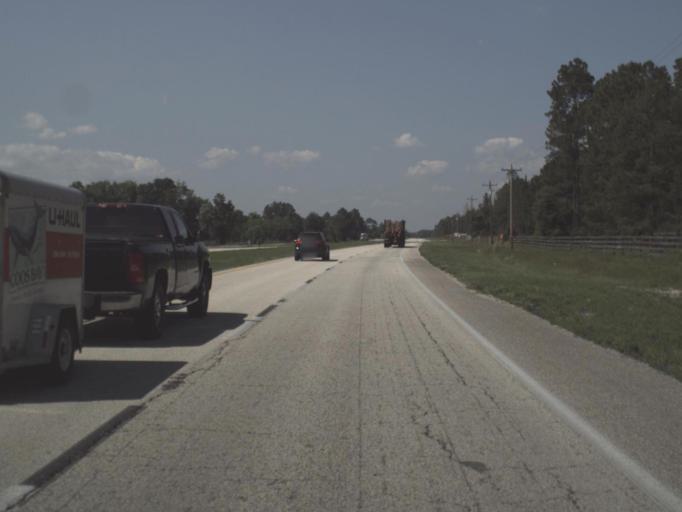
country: US
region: Florida
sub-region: Alachua County
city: Hawthorne
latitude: 29.5508
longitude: -82.0984
